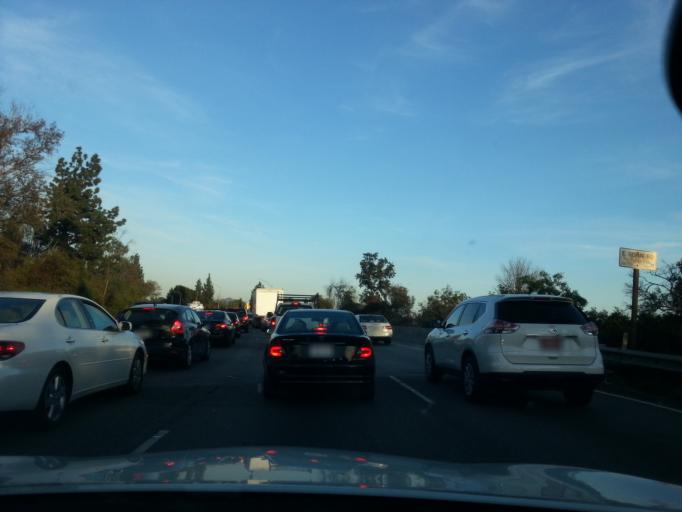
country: US
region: California
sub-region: Los Angeles County
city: Sherman Oaks
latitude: 34.1595
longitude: -118.4683
